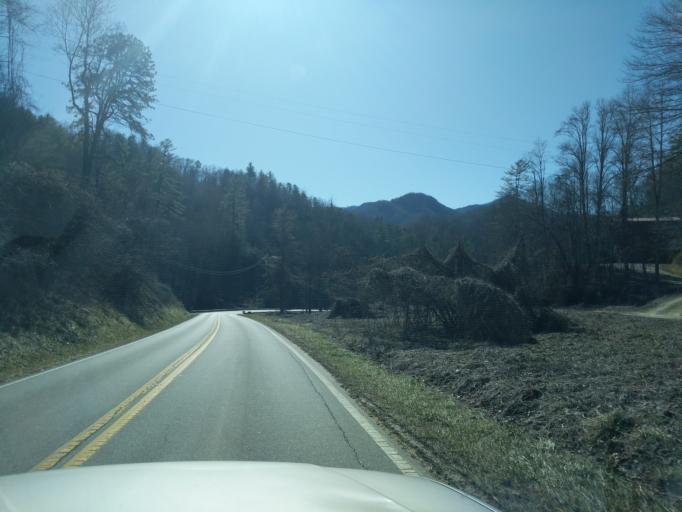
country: US
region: North Carolina
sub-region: Swain County
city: Bryson City
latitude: 35.3332
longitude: -83.5757
